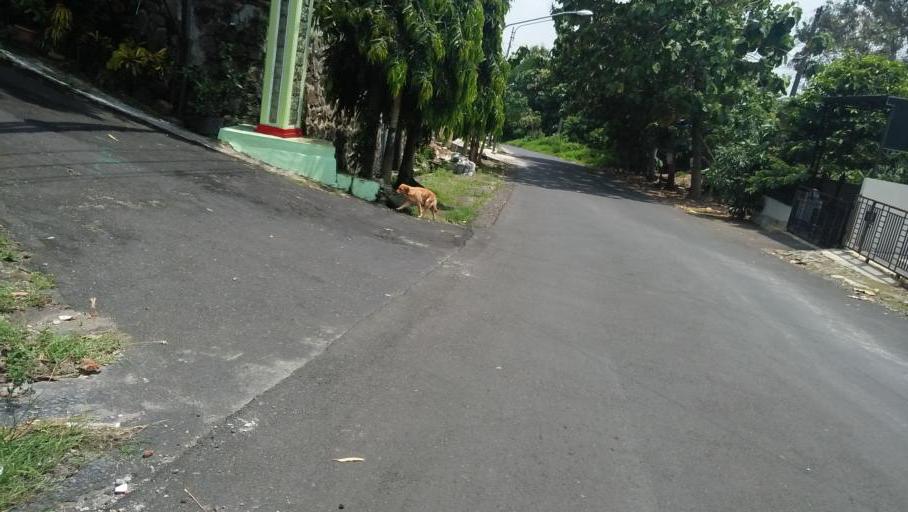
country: ID
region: Central Java
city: Semarang
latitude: -7.0353
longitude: 110.4544
